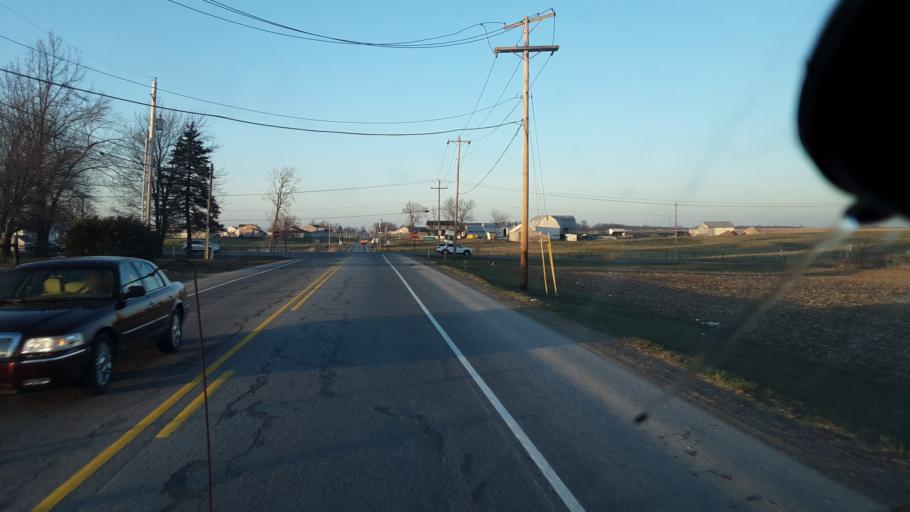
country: US
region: Indiana
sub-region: Allen County
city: Grabill
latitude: 41.2090
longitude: -84.9417
